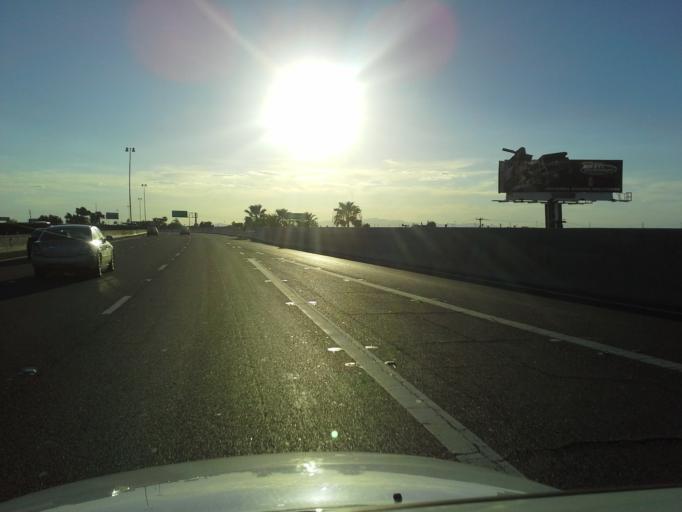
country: US
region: Arizona
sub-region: Maricopa County
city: Phoenix
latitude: 33.4297
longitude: -112.0858
